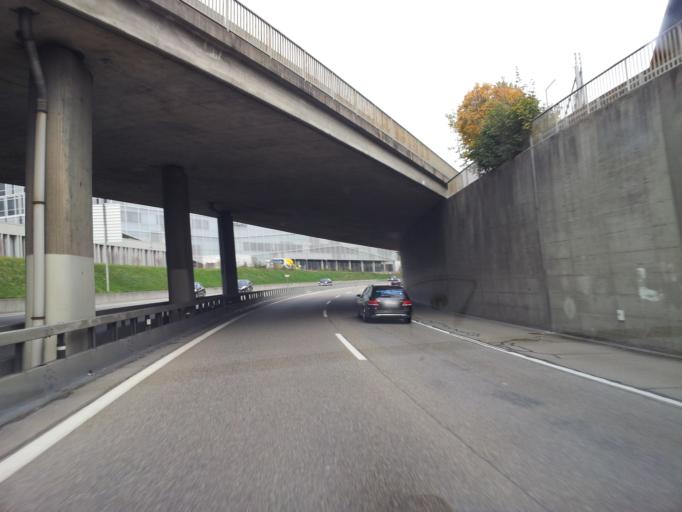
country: CH
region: Bern
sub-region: Bern-Mittelland District
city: Bern
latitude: 46.9567
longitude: 7.4684
